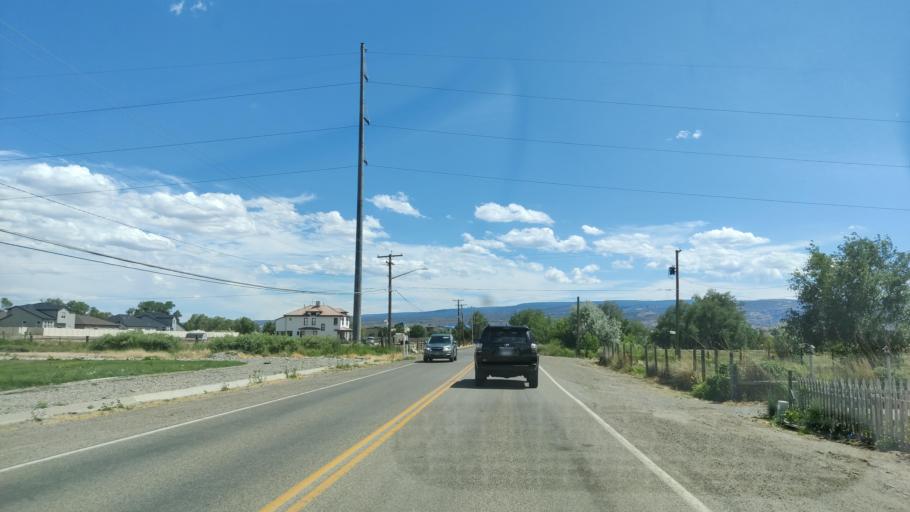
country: US
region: Colorado
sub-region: Mesa County
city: Redlands
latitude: 39.0997
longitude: -108.5988
